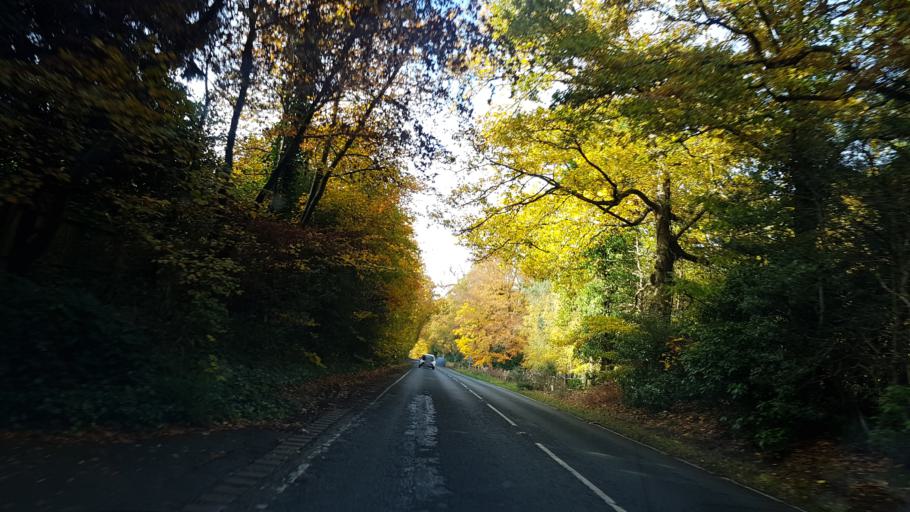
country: GB
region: England
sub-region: Surrey
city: Elstead
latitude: 51.1922
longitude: -0.7282
